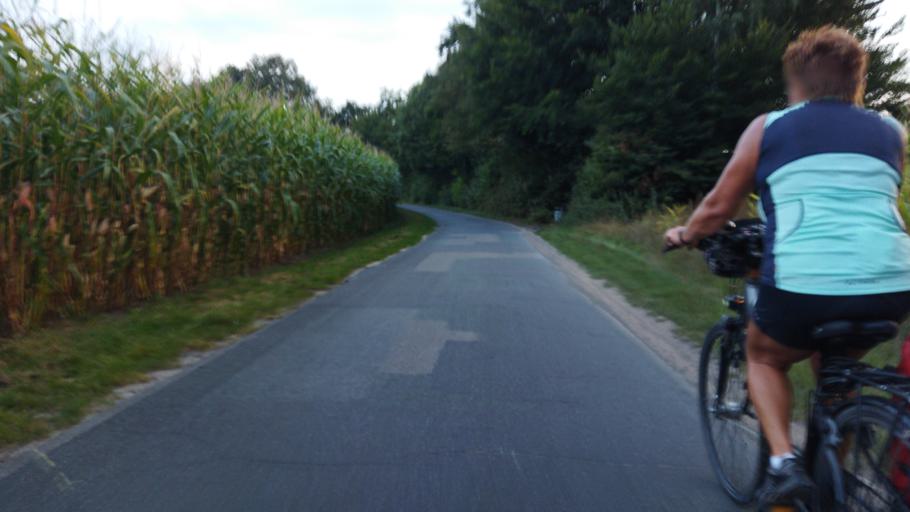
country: DE
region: Lower Saxony
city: Bad Laer
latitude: 52.1165
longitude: 8.0549
